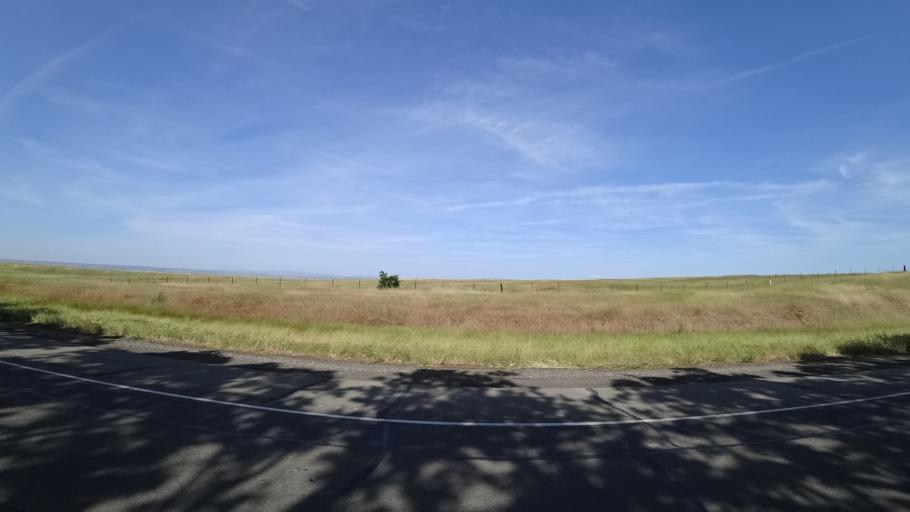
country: US
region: California
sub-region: Tehama County
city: Los Molinos
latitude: 39.9544
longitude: -122.0585
